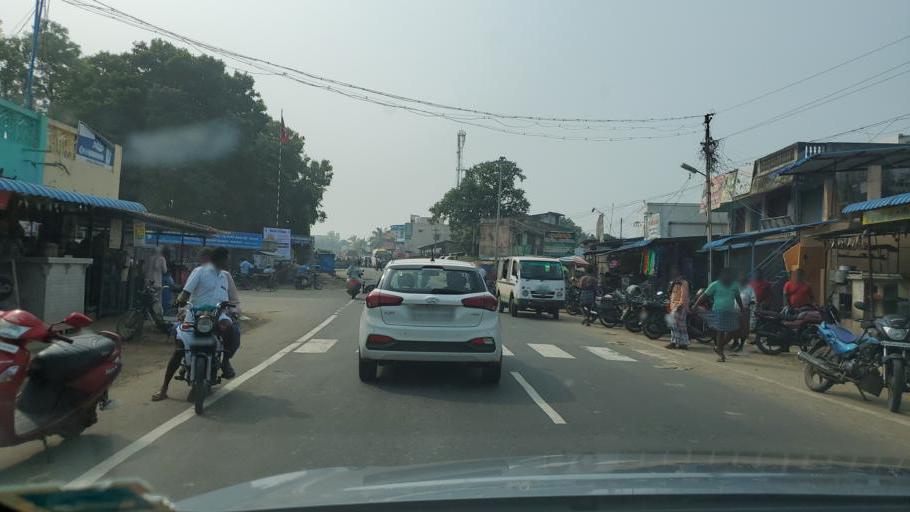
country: IN
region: Tamil Nadu
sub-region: Ariyalur
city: Ariyalur
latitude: 11.2346
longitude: 79.0221
